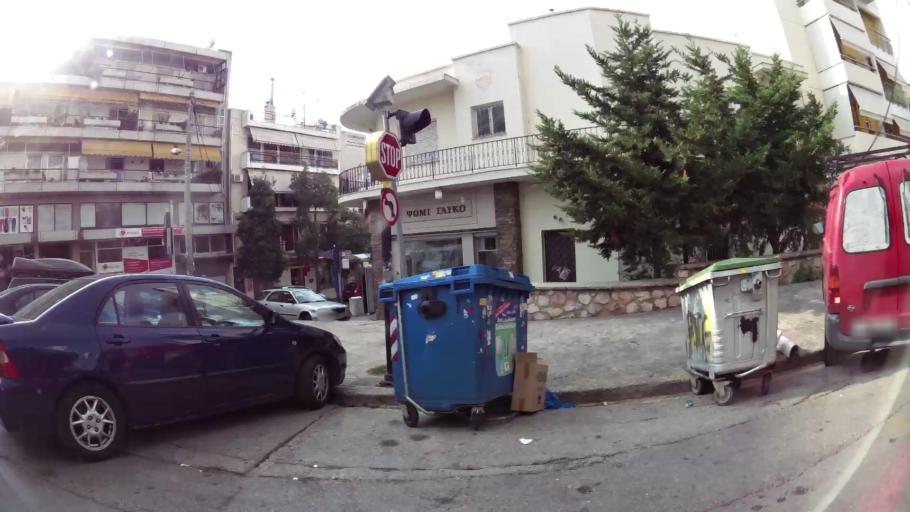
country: GR
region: Attica
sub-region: Nomarchia Athinas
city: Nea Smyrni
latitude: 37.9425
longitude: 23.7215
